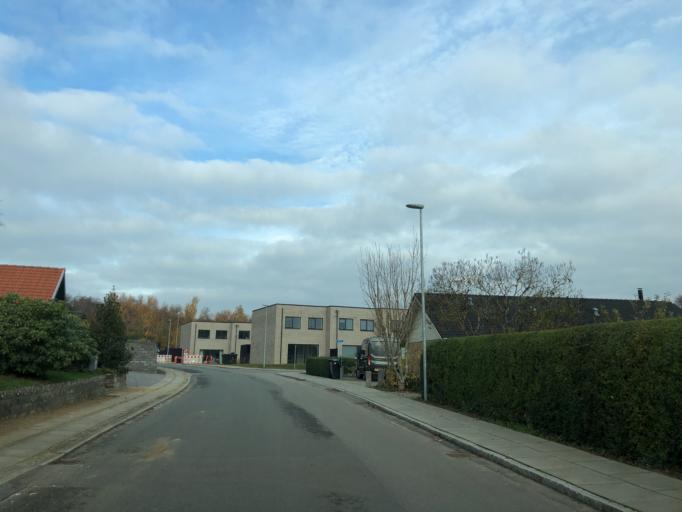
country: DK
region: Central Jutland
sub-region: Silkeborg Kommune
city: Silkeborg
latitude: 56.1501
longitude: 9.4903
